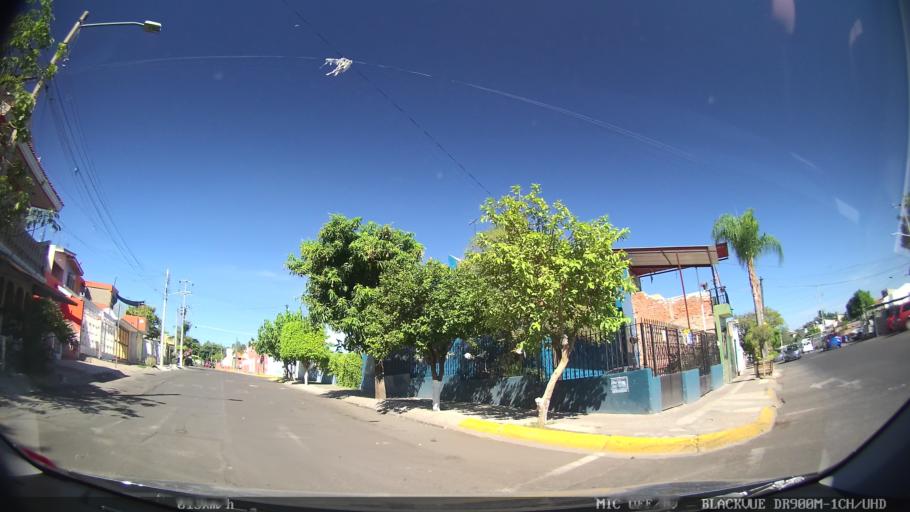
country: MX
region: Jalisco
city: Tlaquepaque
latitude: 20.6806
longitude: -103.2709
